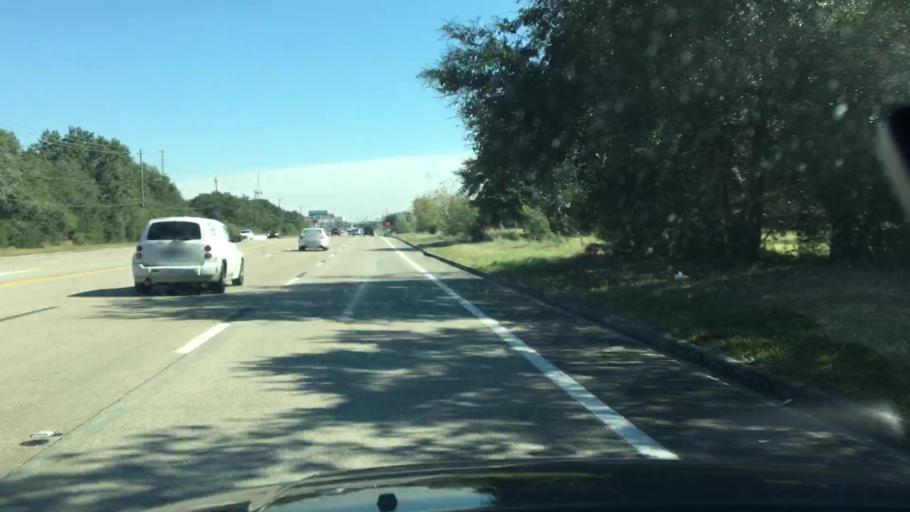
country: US
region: Texas
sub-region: Harris County
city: Webster
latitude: 29.5237
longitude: -95.1475
